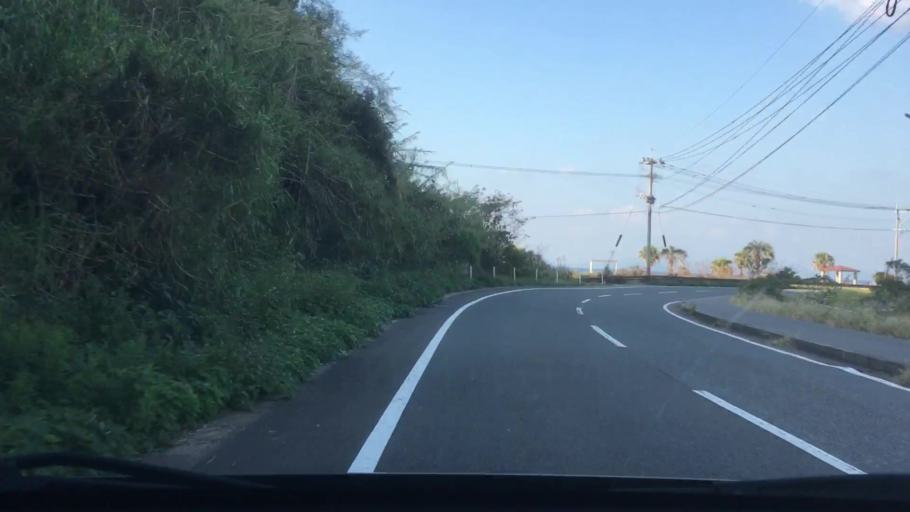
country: JP
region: Nagasaki
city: Sasebo
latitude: 33.0264
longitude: 129.5776
